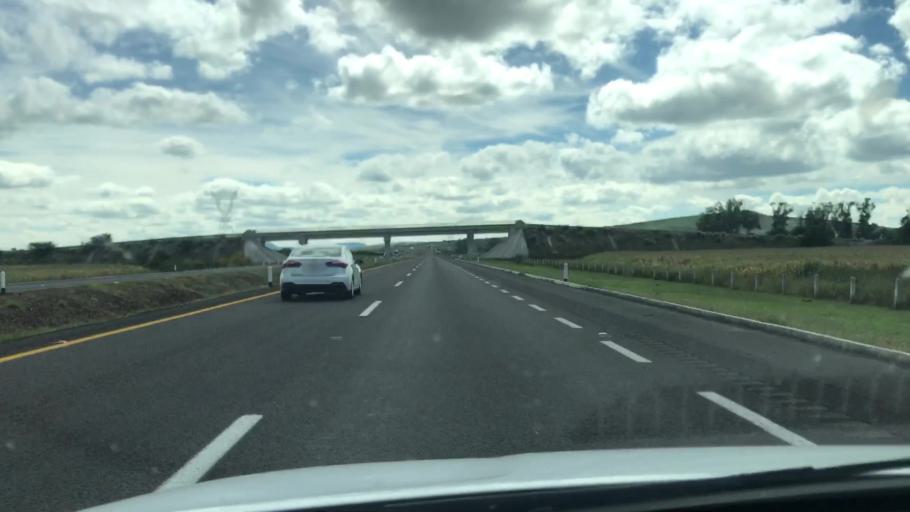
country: MX
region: Guanajuato
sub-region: Irapuato
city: Serrano
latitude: 20.7620
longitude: -101.3838
